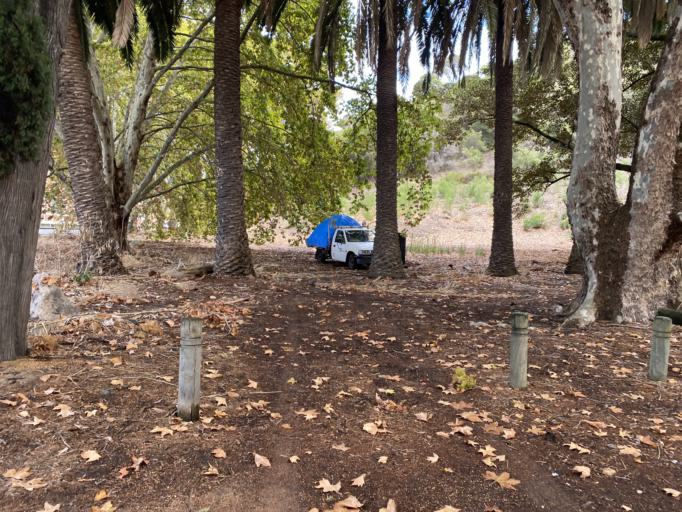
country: AU
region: Western Australia
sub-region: City of Perth
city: West Perth
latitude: -31.9635
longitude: 115.8418
